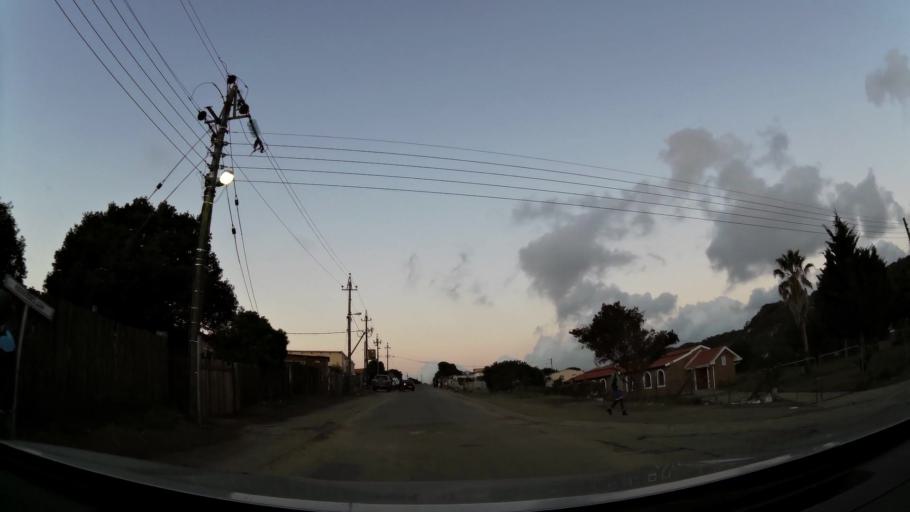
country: ZA
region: Western Cape
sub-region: Eden District Municipality
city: Knysna
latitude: -34.0258
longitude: 22.8157
